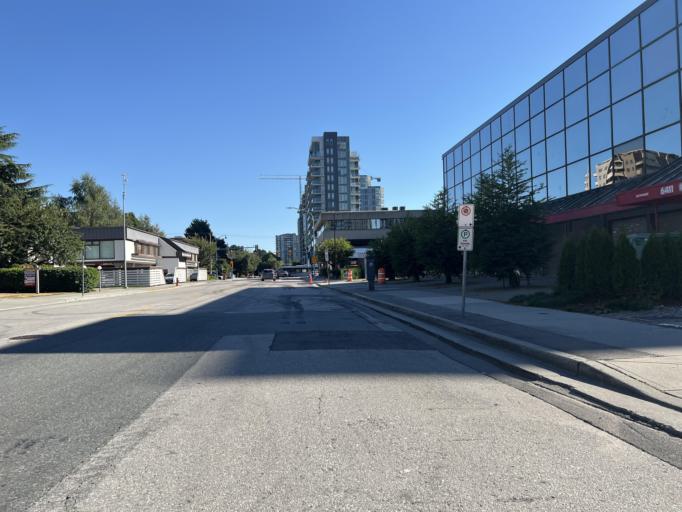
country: CA
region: British Columbia
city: Richmond
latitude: 49.1676
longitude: -123.1338
